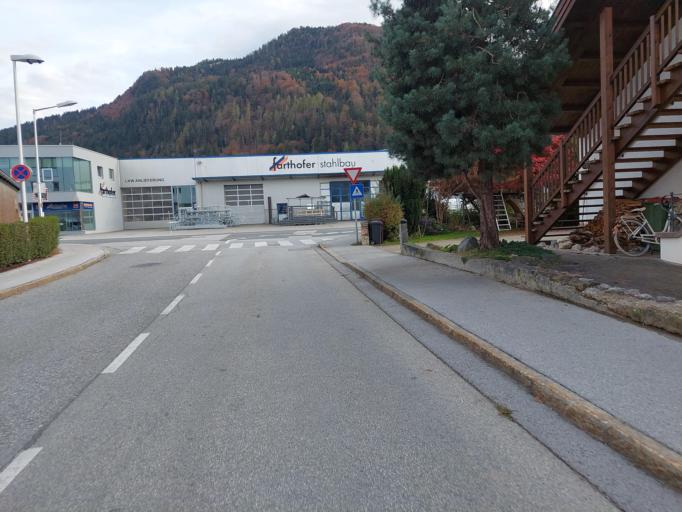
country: AT
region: Tyrol
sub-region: Politischer Bezirk Kufstein
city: Worgl
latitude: 47.4872
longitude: 12.0756
